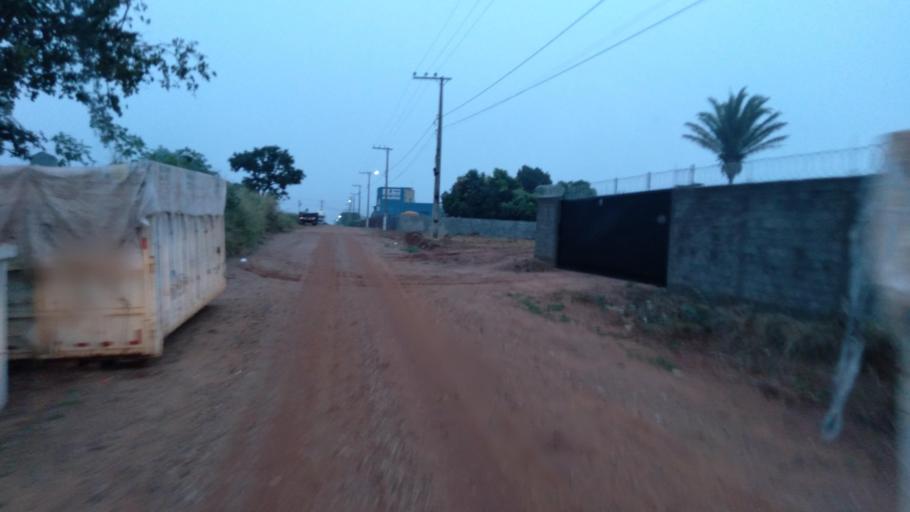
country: BR
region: Goias
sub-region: Mineiros
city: Mineiros
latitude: -17.5815
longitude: -52.5454
